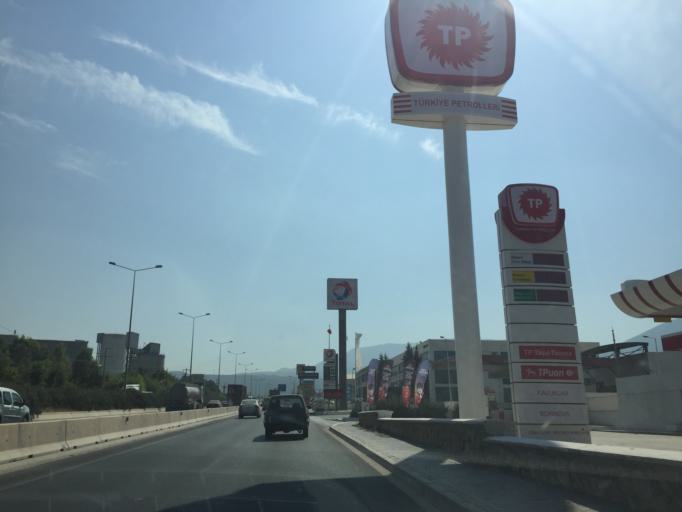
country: TR
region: Izmir
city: Bornova
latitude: 38.4547
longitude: 27.2591
